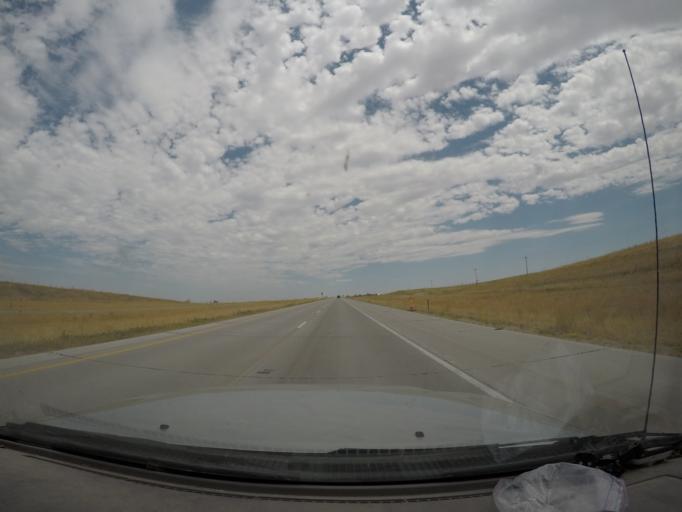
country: US
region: Nebraska
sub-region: Cheyenne County
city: Sidney
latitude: 41.1133
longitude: -102.9868
